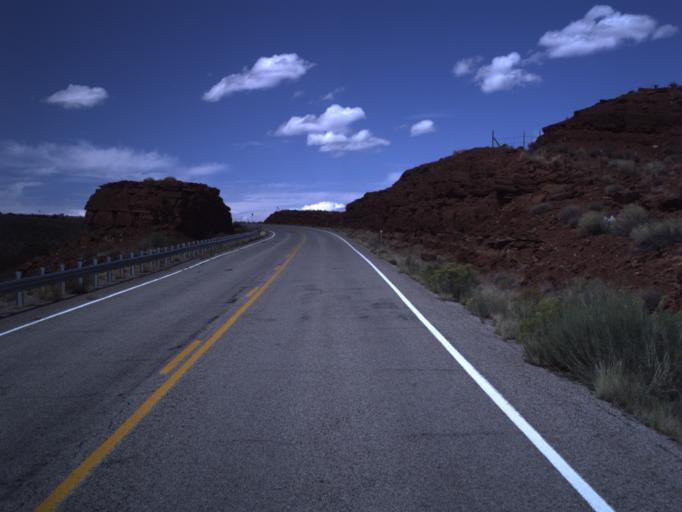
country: US
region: Utah
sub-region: San Juan County
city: Blanding
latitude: 37.2829
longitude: -109.6898
